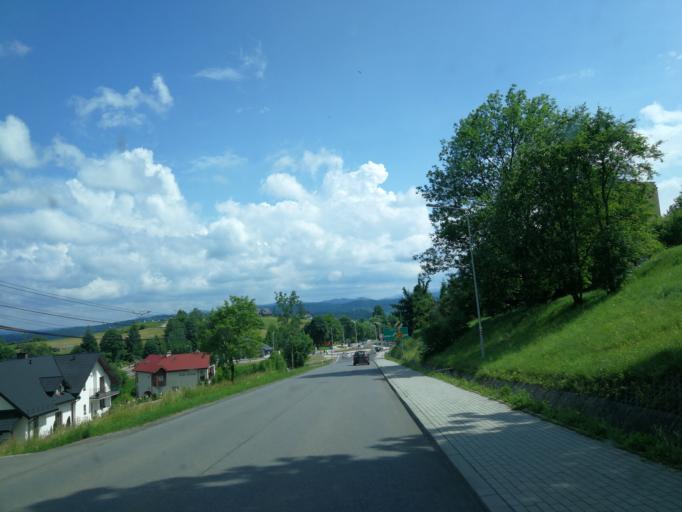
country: PL
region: Subcarpathian Voivodeship
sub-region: Powiat leski
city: Polanczyk
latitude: 49.3712
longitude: 22.4198
